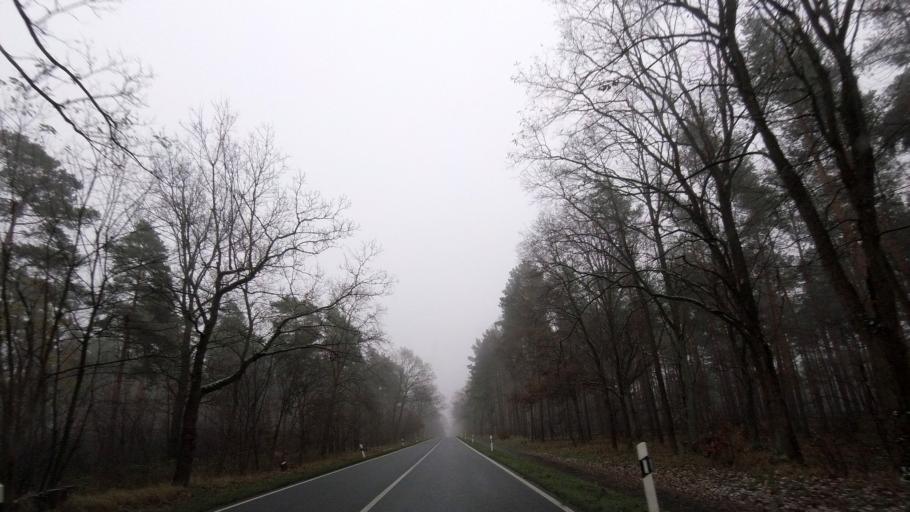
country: DE
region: Brandenburg
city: Niedergorsdorf
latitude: 52.0334
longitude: 12.9497
